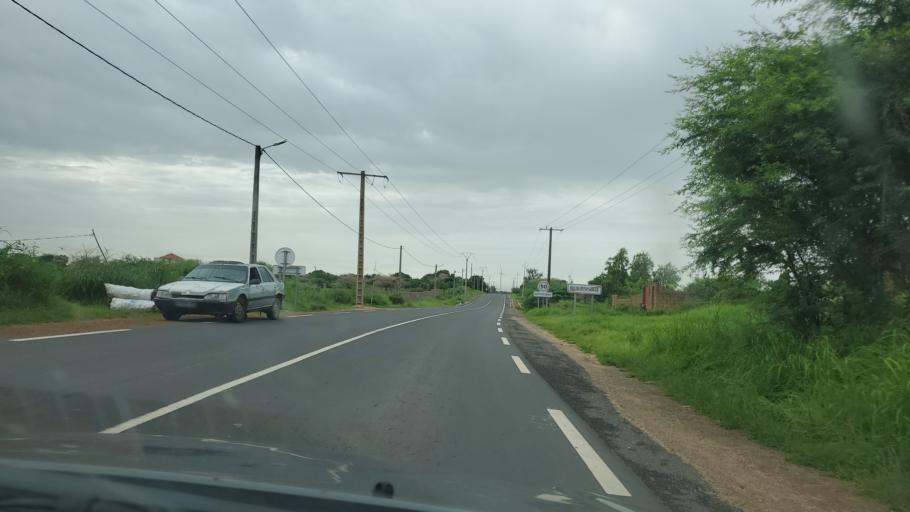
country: SN
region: Thies
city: Kayar
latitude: 15.1040
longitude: -16.9141
